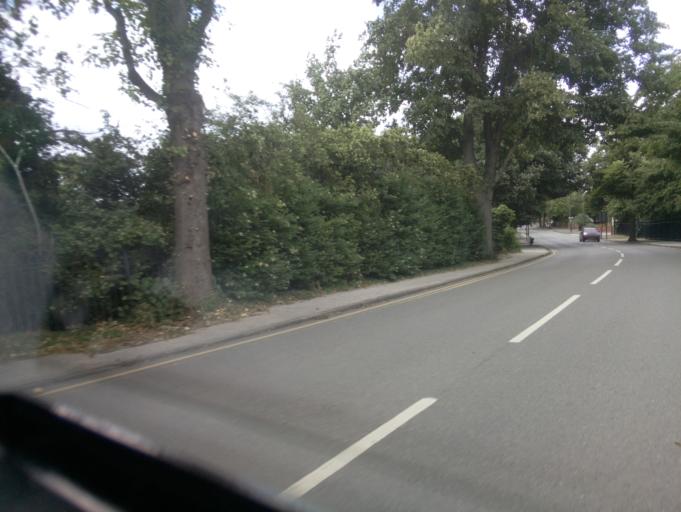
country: GB
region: England
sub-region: Warwickshire
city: Nuneaton
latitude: 52.5258
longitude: -1.4600
